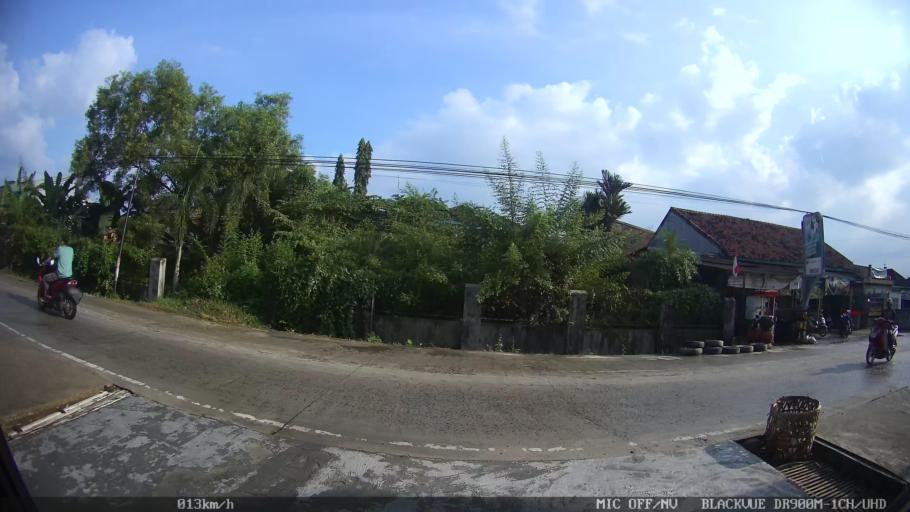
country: ID
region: Lampung
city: Kedaton
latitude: -5.3857
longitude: 105.3131
